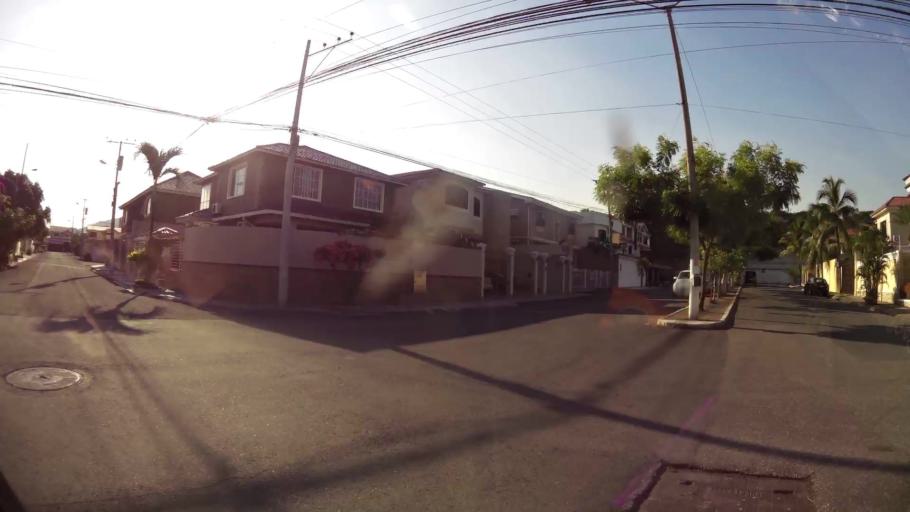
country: EC
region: Guayas
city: Santa Lucia
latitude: -2.1866
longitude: -79.9709
